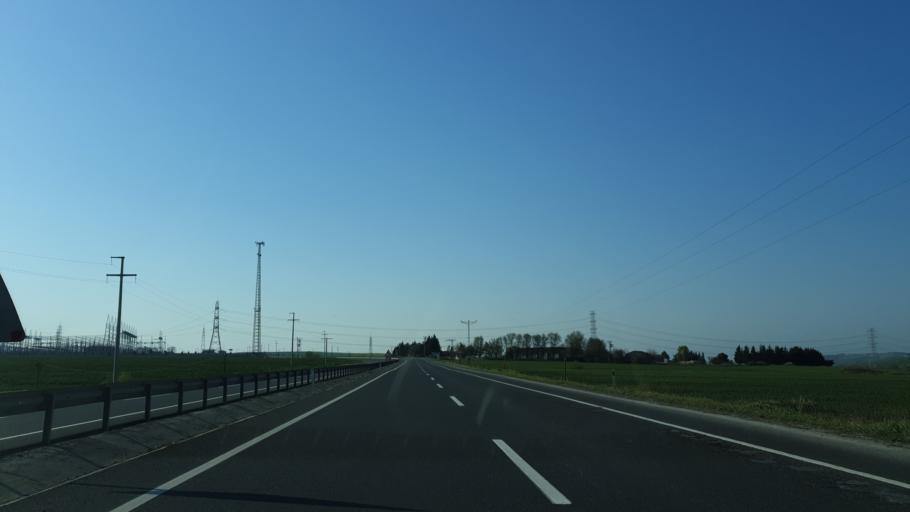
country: TR
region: Tekirdag
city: Corlu
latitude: 41.1108
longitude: 27.7492
